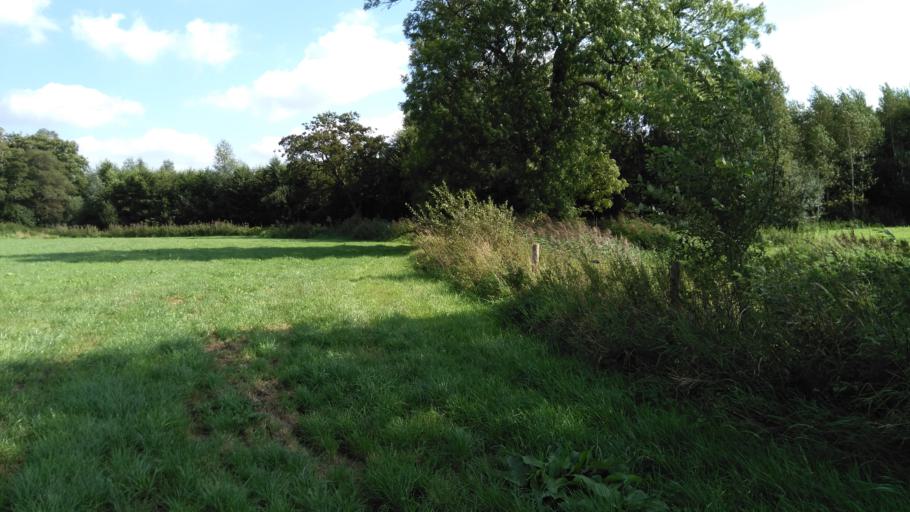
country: BE
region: Flanders
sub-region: Provincie Antwerpen
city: Baarle-Hertog
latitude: 51.4810
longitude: 4.8415
